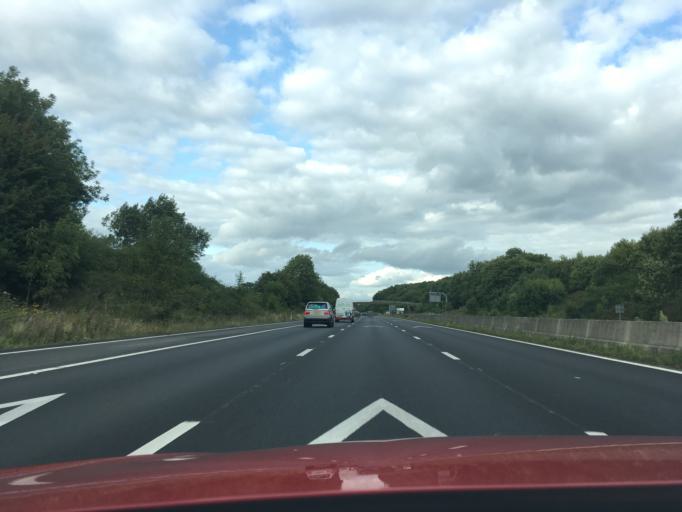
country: GB
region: England
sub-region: Gloucestershire
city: Barnwood
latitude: 51.8246
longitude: -2.2164
